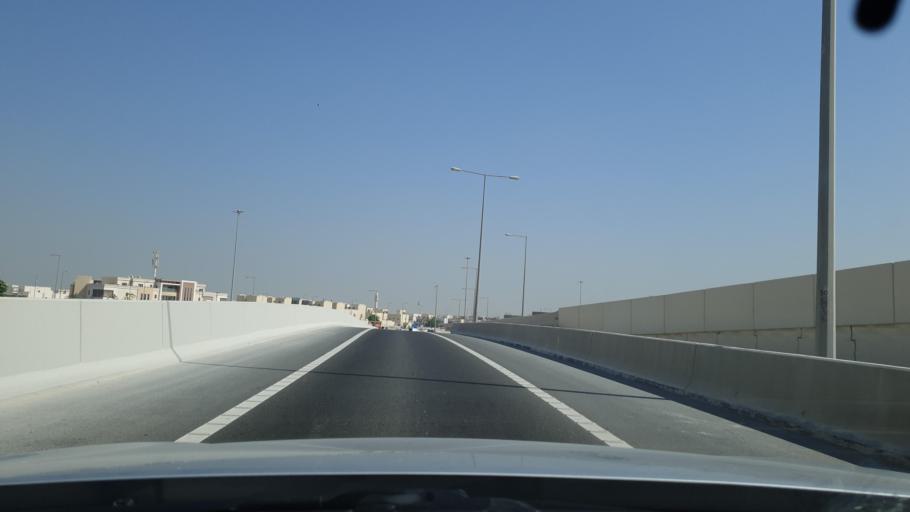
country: QA
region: Baladiyat ad Dawhah
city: Doha
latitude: 25.2200
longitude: 51.5367
